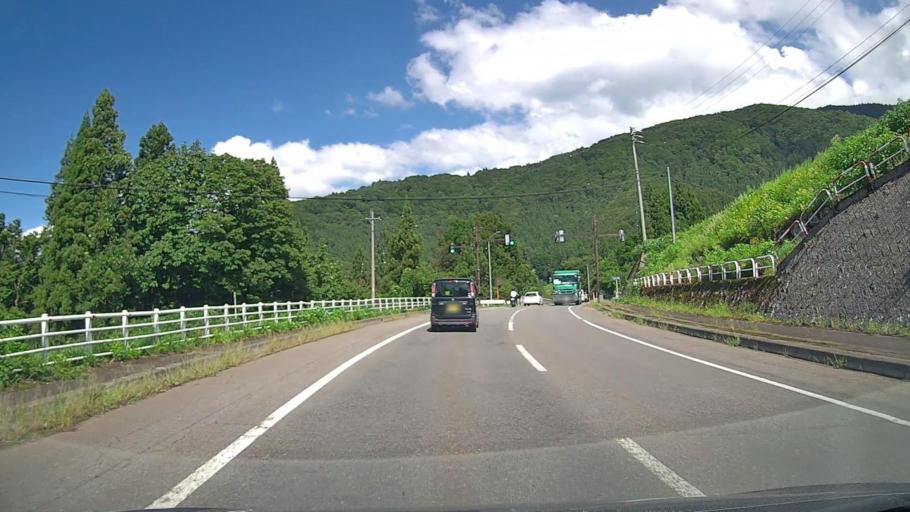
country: JP
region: Nagano
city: Iiyama
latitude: 36.9564
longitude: 138.4444
